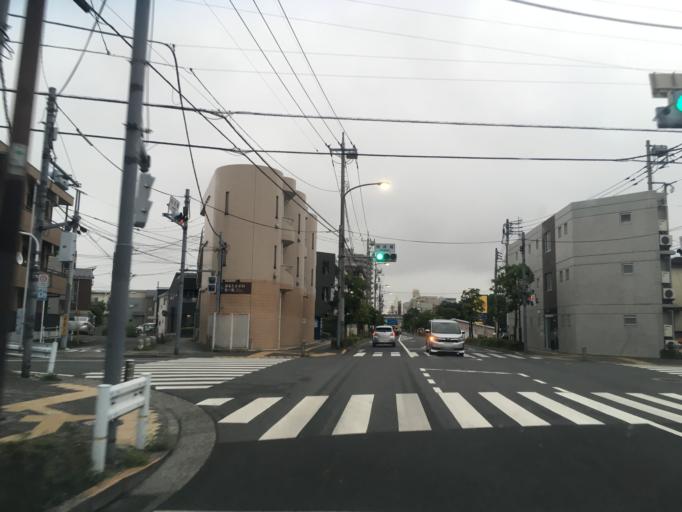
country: JP
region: Tokyo
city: Chofugaoka
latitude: 35.6470
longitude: 139.5348
